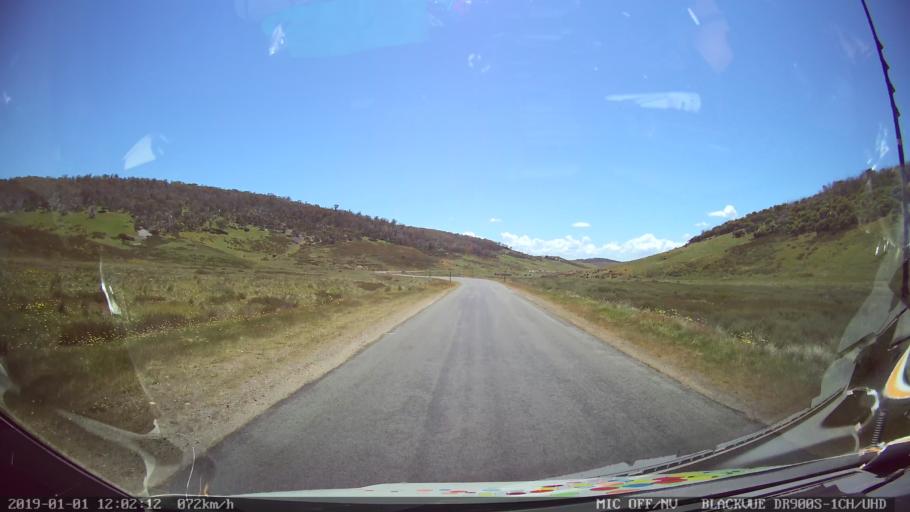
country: AU
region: New South Wales
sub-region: Snowy River
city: Jindabyne
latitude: -35.8742
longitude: 148.4746
